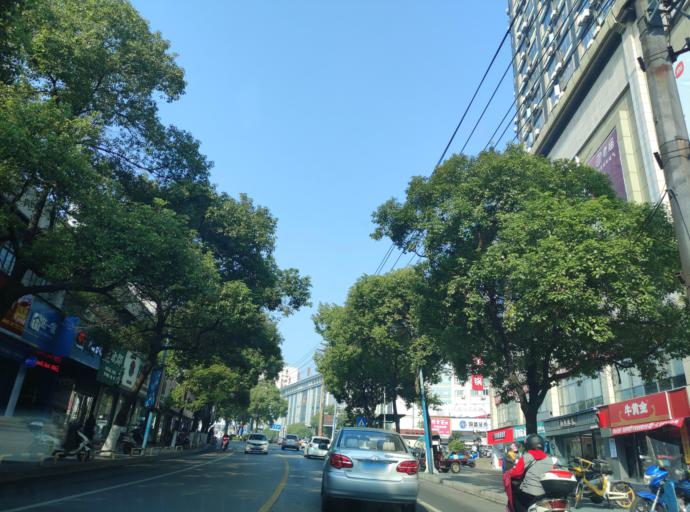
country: CN
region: Jiangxi Sheng
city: Pingxiang
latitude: 27.6327
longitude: 113.8464
